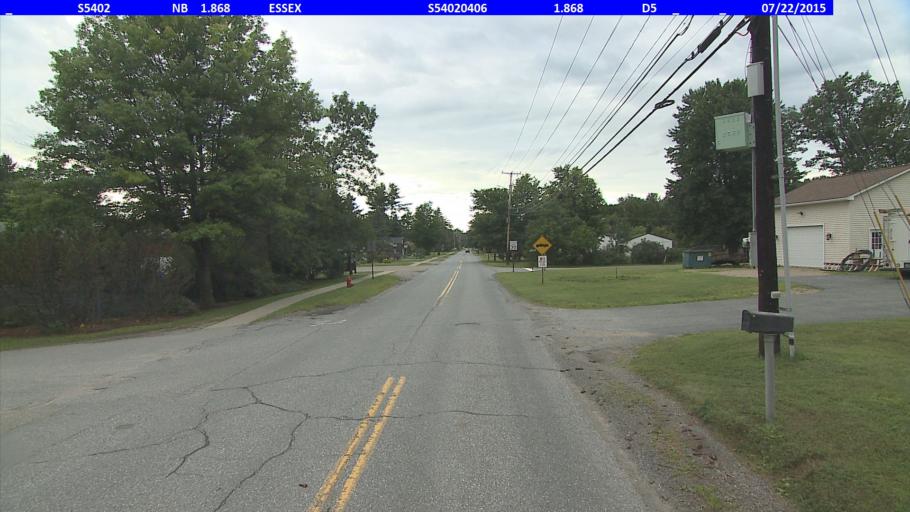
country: US
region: Vermont
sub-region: Chittenden County
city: Jericho
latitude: 44.5045
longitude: -73.0520
